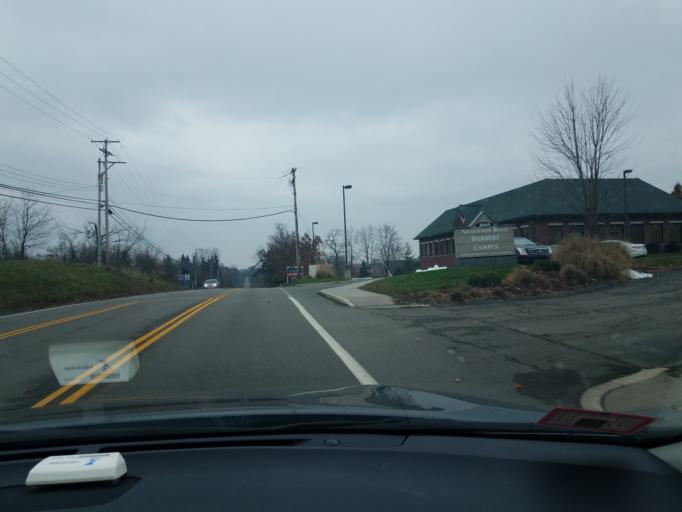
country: US
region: Pennsylvania
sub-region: Allegheny County
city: Franklin Park
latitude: 40.6116
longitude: -80.0999
